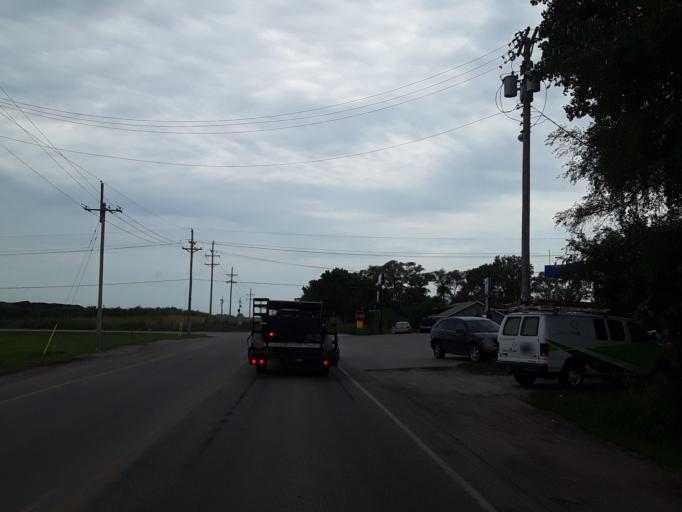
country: US
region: Nebraska
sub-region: Saunders County
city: Yutan
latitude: 41.2348
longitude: -96.3304
